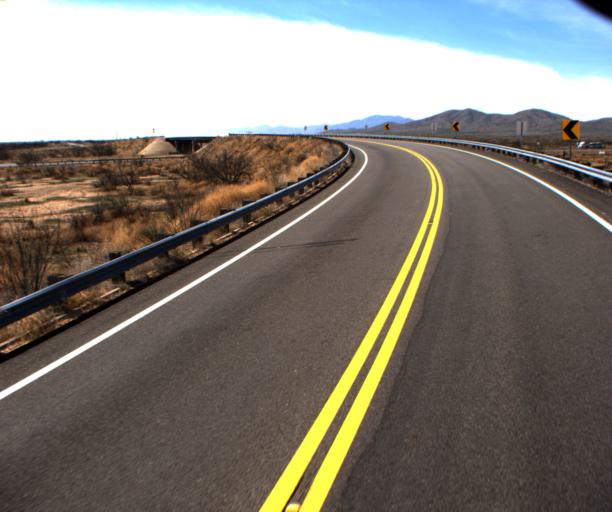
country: US
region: Arizona
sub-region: Cochise County
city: Willcox
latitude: 32.1783
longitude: -109.9498
